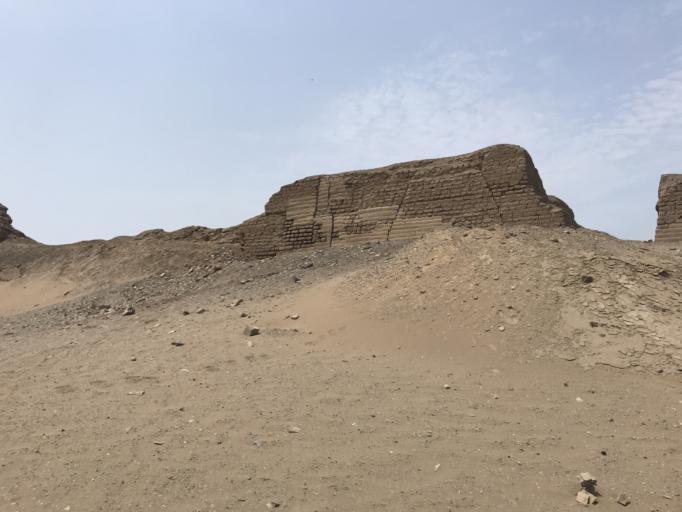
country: PE
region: Lima
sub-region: Lima
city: Punta Hermosa
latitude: -12.2546
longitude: -76.8985
